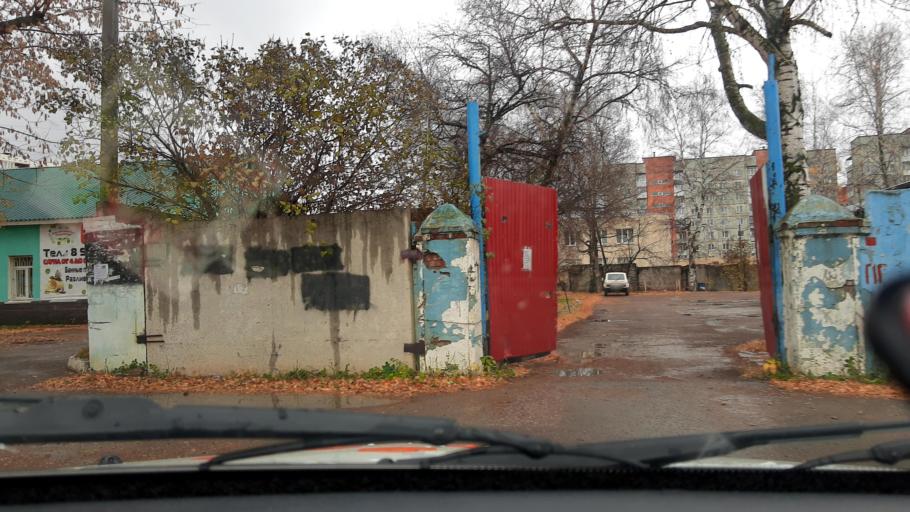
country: RU
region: Bashkortostan
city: Iglino
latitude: 54.7695
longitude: 56.2257
